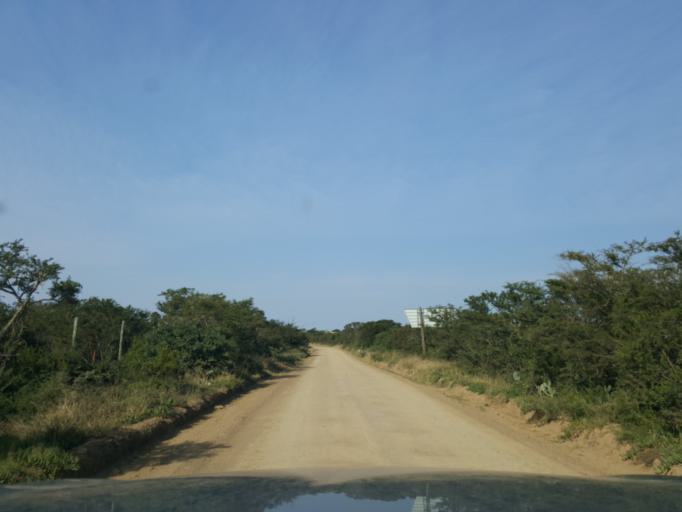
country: ZA
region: Eastern Cape
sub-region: Cacadu District Municipality
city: Grahamstown
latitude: -33.4181
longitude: 26.3175
